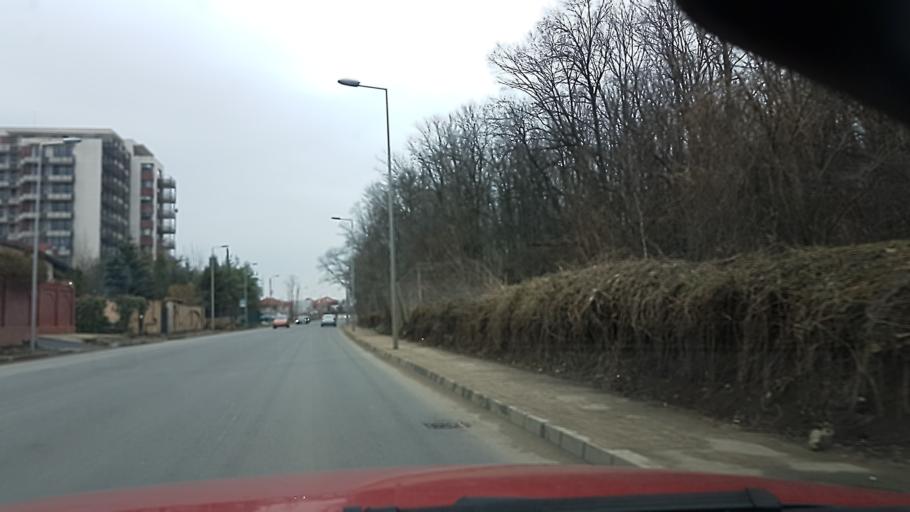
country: RO
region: Ilfov
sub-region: Comuna Tunari
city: Tunari
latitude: 44.5236
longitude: 26.1433
